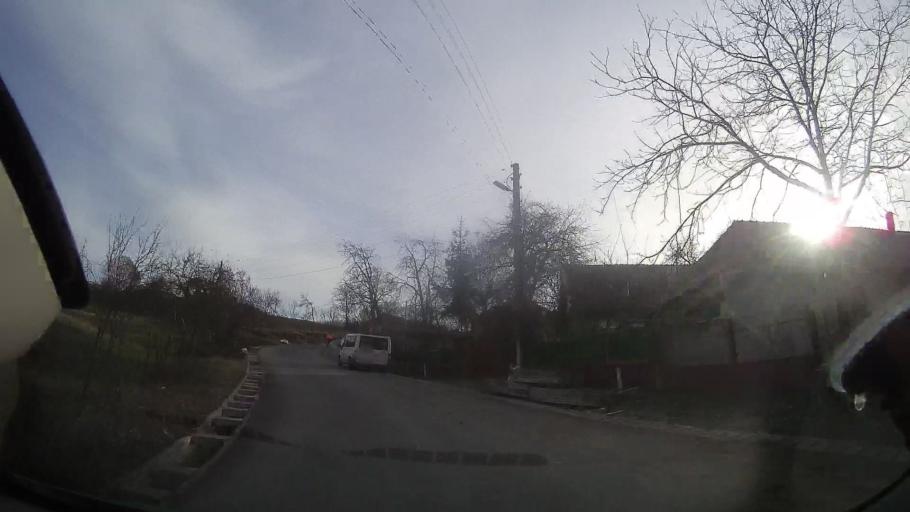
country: RO
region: Bihor
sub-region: Comuna Sarbi
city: Burzuc
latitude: 47.1389
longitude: 22.1831
